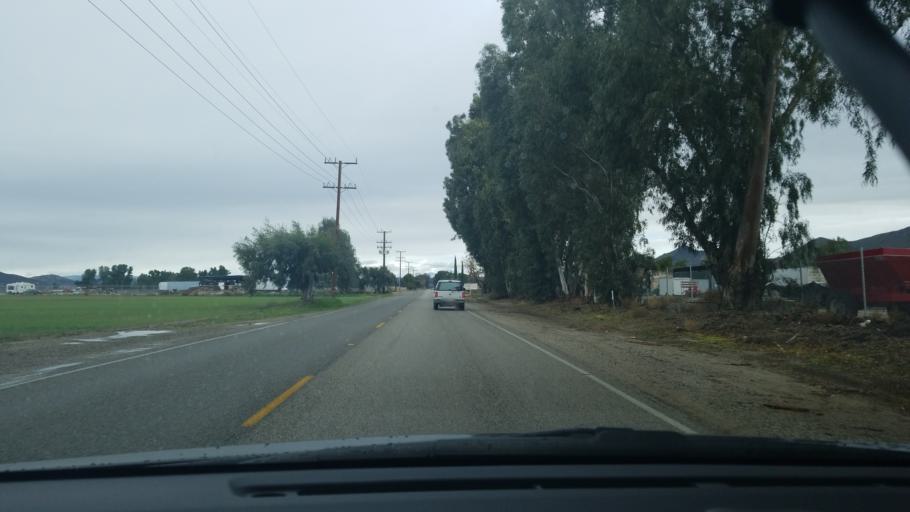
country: US
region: California
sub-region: Riverside County
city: Winchester
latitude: 33.7074
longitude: -117.0660
